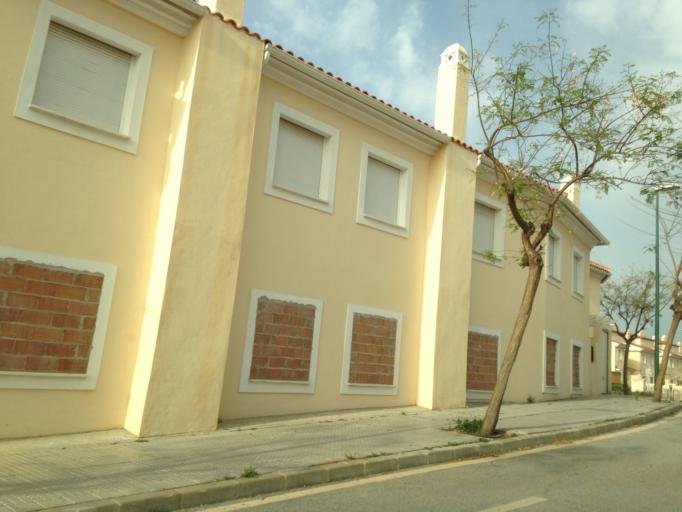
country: ES
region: Andalusia
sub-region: Provincia de Malaga
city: Estacion de Cartama
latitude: 36.7353
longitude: -4.5659
